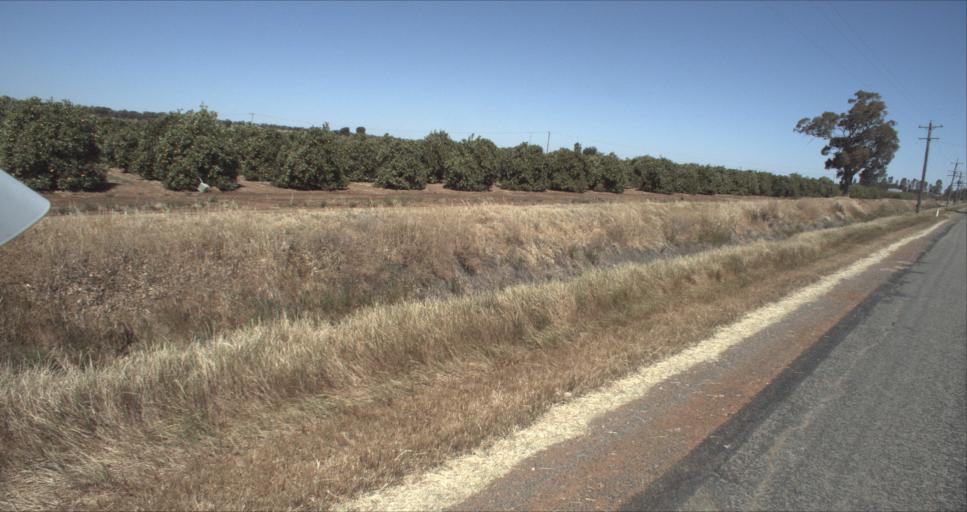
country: AU
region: New South Wales
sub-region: Leeton
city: Leeton
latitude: -34.4727
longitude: 146.4166
